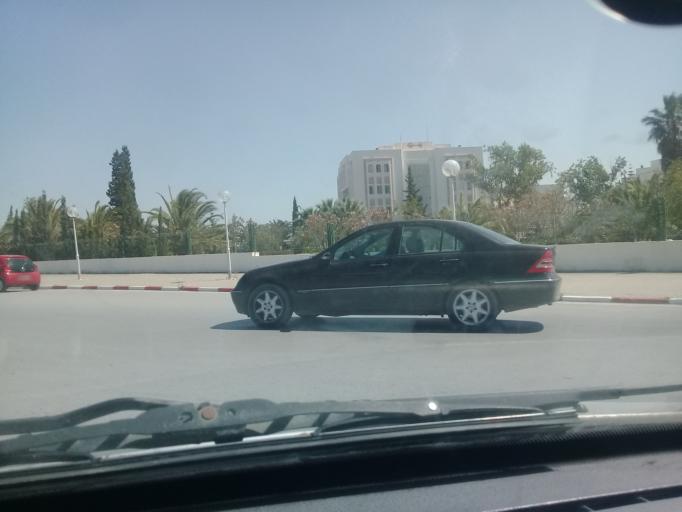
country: TN
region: Ariana
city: Ariana
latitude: 36.8349
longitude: 10.2384
